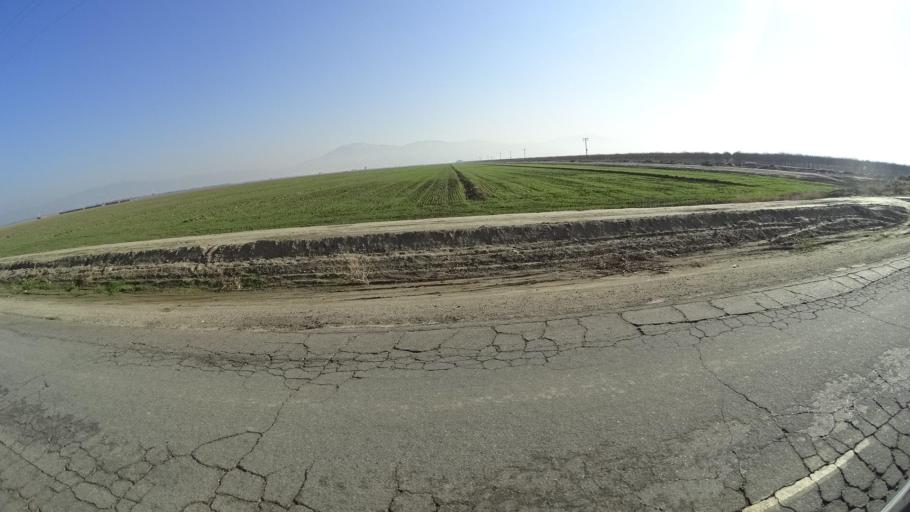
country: US
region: California
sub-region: Kern County
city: Weedpatch
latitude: 35.1516
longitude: -118.9677
